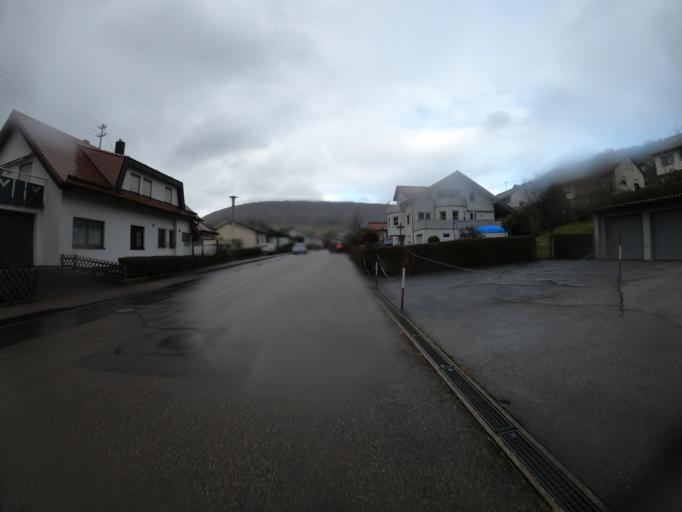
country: DE
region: Baden-Wuerttemberg
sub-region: Regierungsbezirk Stuttgart
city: Donzdorf
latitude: 48.7134
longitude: 9.8605
